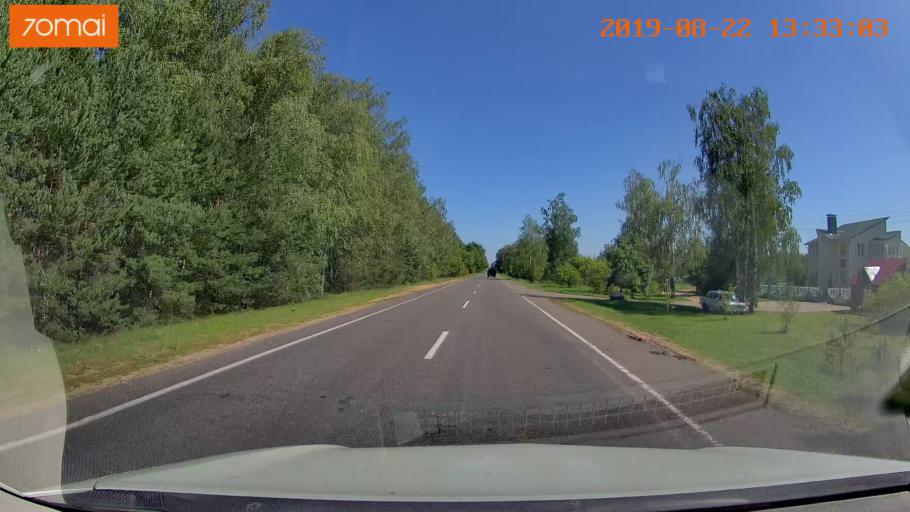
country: BY
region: Minsk
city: Staryya Darohi
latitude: 53.2168
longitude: 28.2179
